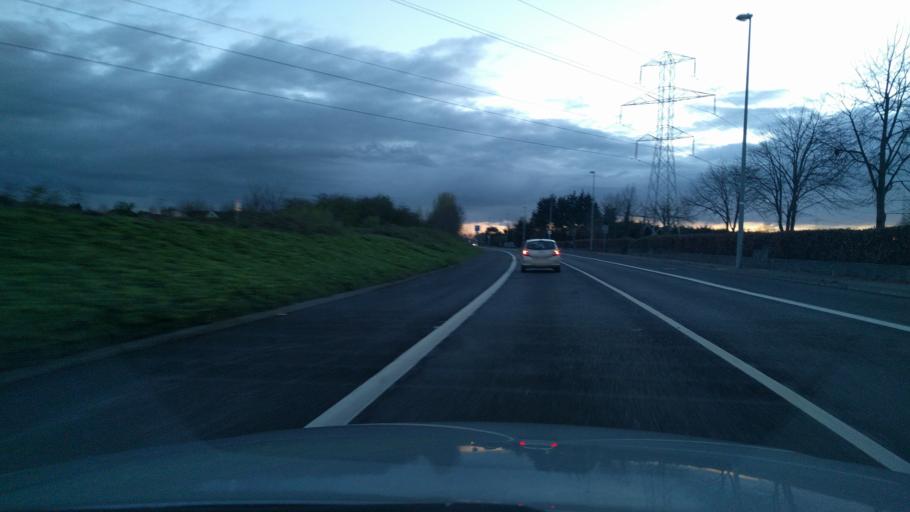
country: IE
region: Leinster
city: Clondalkin
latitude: 53.3273
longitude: -6.3976
